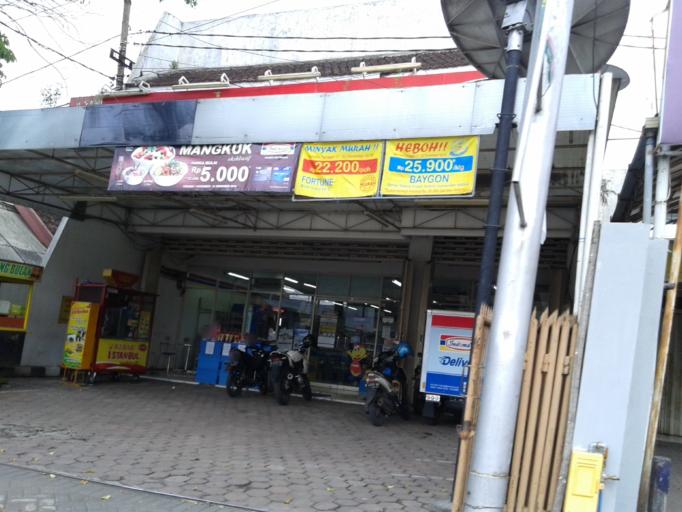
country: ID
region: East Java
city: Malang
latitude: -7.9357
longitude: 112.6455
